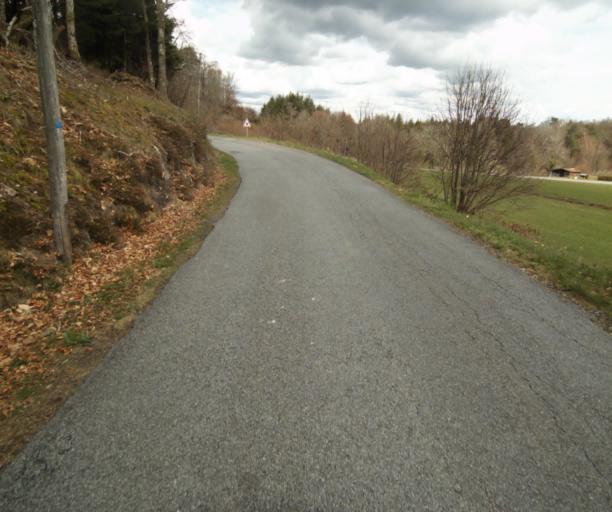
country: FR
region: Limousin
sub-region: Departement de la Correze
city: Correze
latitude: 45.3269
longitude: 1.9542
